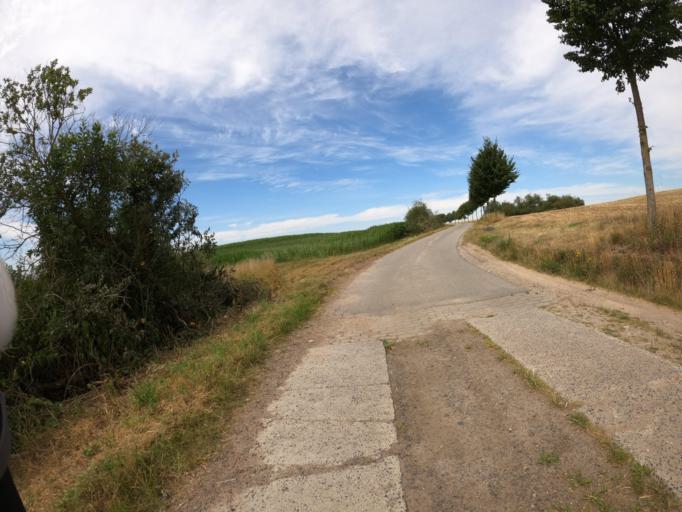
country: DE
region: Mecklenburg-Vorpommern
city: Woldegk
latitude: 53.4511
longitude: 13.4999
